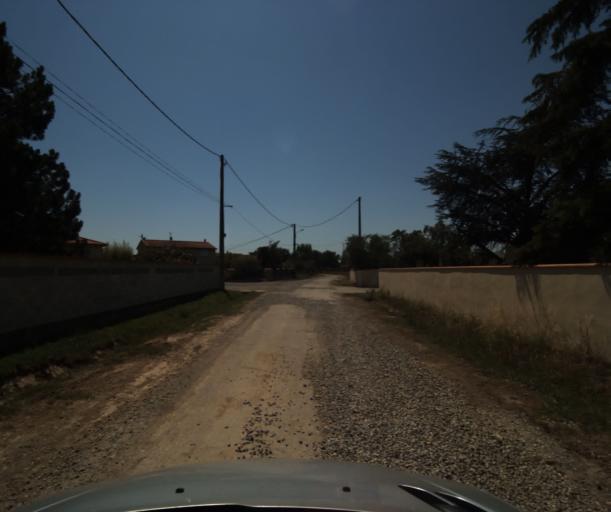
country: FR
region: Midi-Pyrenees
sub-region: Departement de la Haute-Garonne
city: Saubens
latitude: 43.4756
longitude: 1.3673
